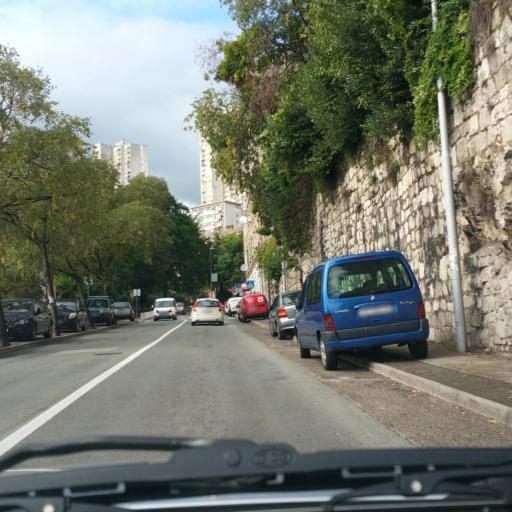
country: HR
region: Primorsko-Goranska
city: Drenova
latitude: 45.3357
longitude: 14.4330
